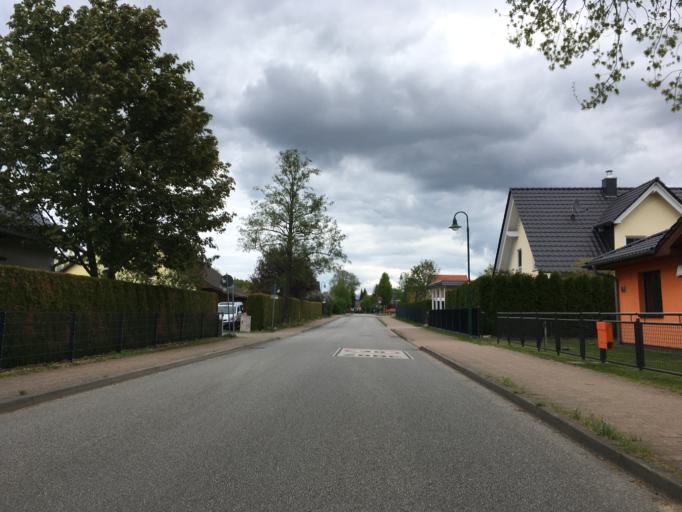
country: DE
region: Berlin
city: Buch
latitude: 52.6560
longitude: 13.5173
